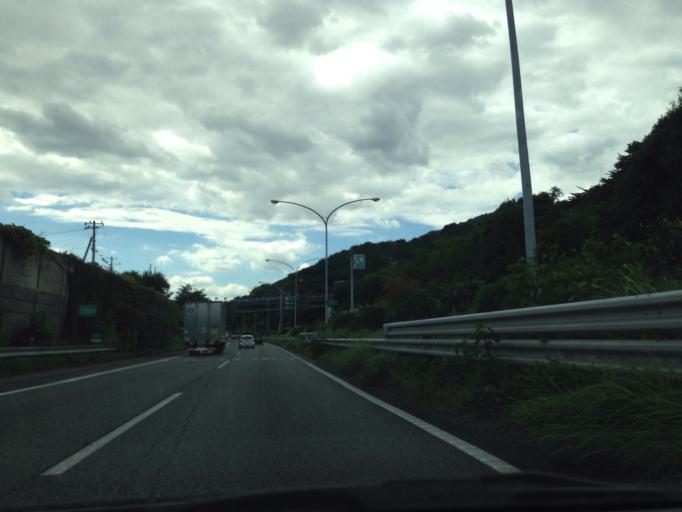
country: JP
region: Kanagawa
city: Hadano
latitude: 35.3523
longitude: 139.1260
